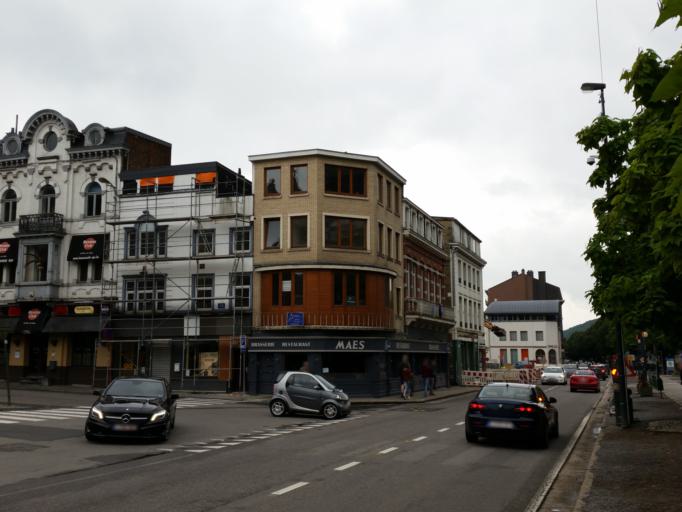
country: BE
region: Wallonia
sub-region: Province de Liege
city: Spa
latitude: 50.4925
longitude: 5.8642
